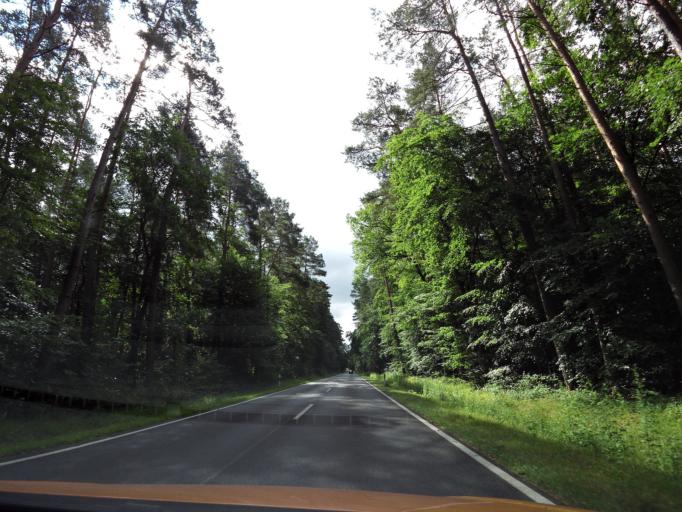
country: DE
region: Mecklenburg-Vorpommern
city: Muhl Rosin
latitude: 53.7502
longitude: 12.2544
